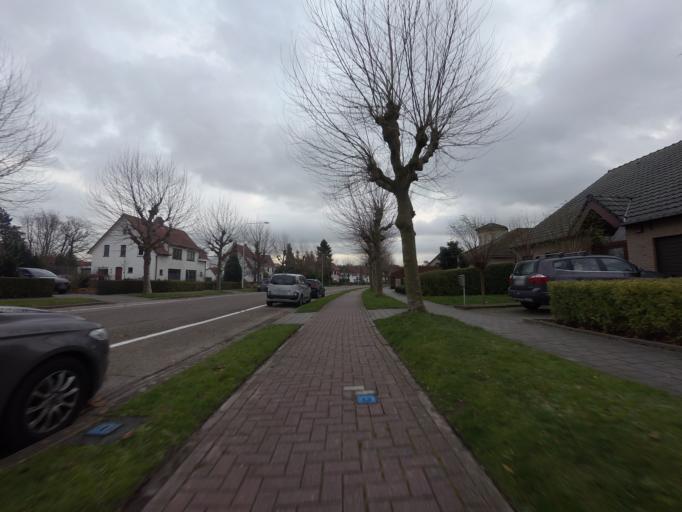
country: BE
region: Flanders
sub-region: Provincie Antwerpen
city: Hemiksem
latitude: 51.1493
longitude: 4.3503
